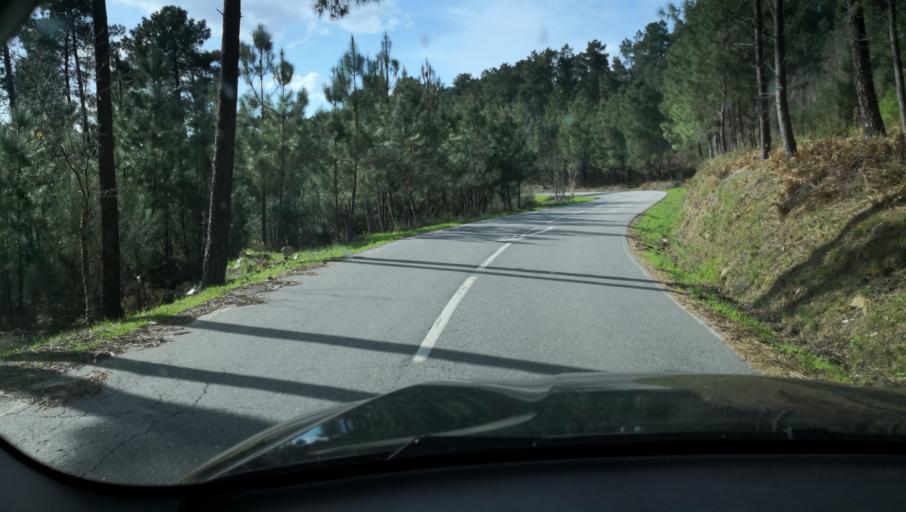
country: PT
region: Vila Real
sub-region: Vila Real
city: Vila Real
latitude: 41.2758
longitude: -7.6732
